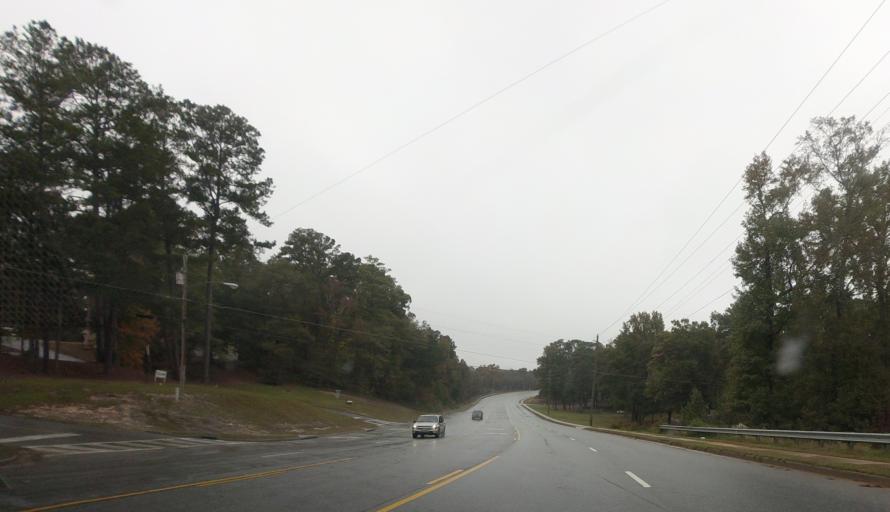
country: US
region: Georgia
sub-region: Houston County
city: Centerville
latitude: 32.6091
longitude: -83.6659
